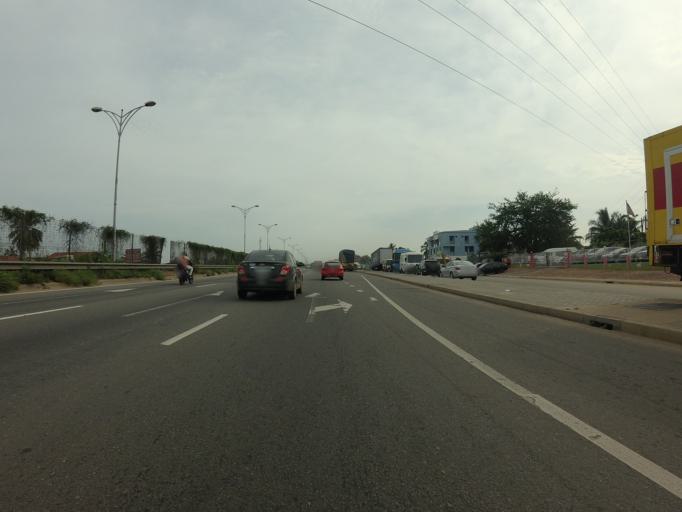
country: GH
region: Greater Accra
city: Gbawe
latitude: 5.5793
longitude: -0.2782
